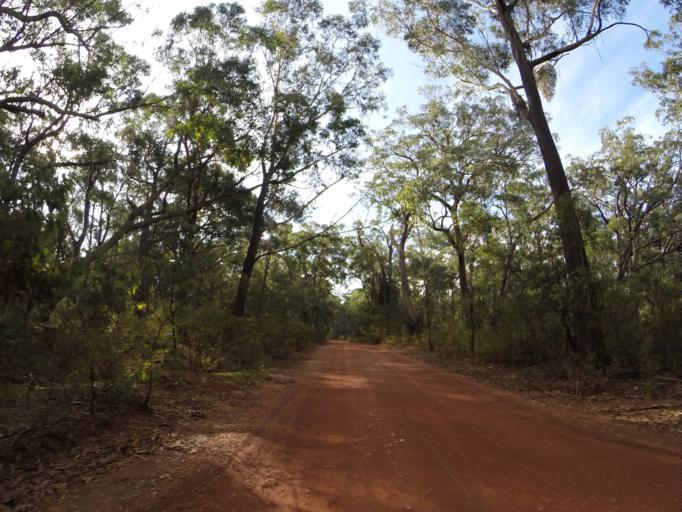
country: AU
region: New South Wales
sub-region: Wingecarribee
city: Bundanoon
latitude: -34.5267
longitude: 150.2133
